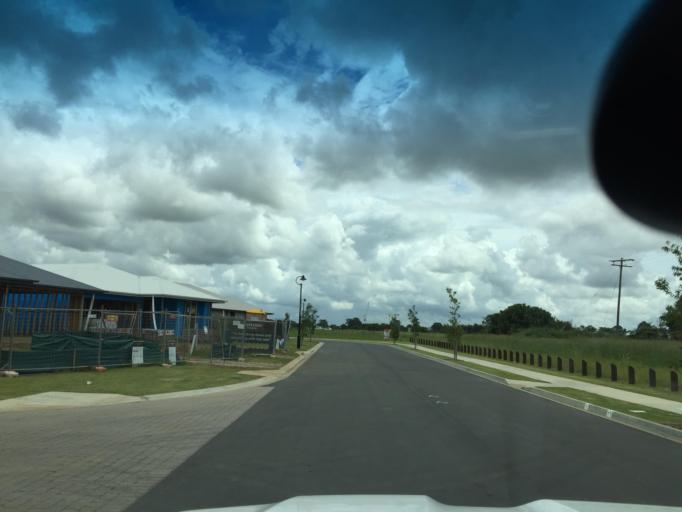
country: AU
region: Queensland
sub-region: Moreton Bay
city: Caboolture South
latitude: -27.0936
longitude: 152.9666
